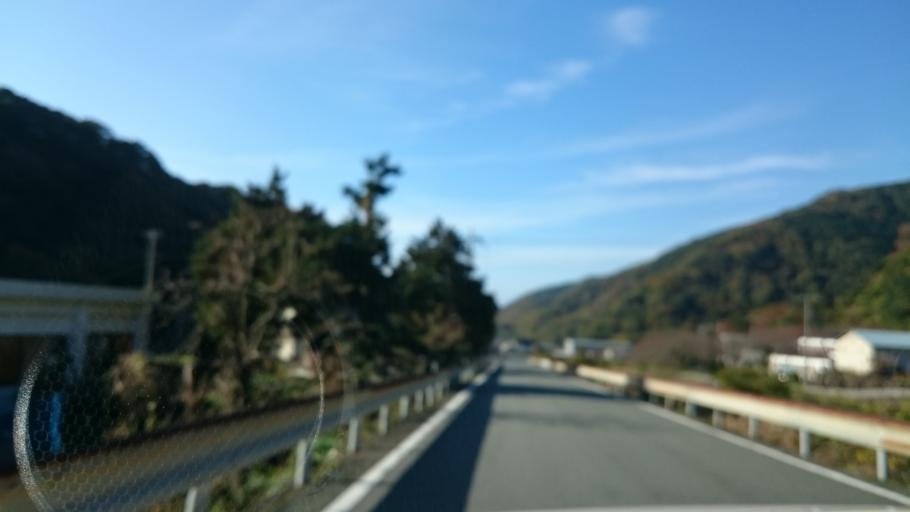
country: JP
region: Shizuoka
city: Heda
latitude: 34.9667
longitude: 138.8031
